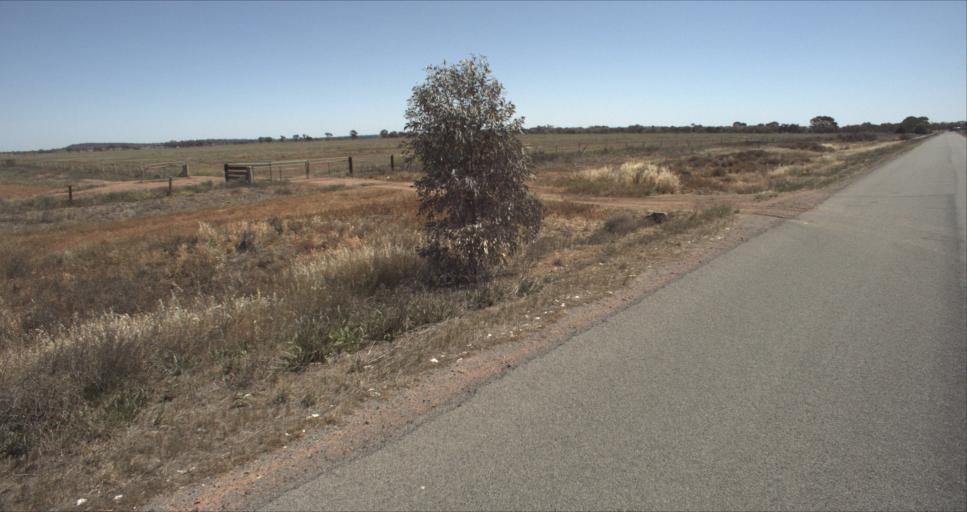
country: AU
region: New South Wales
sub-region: Leeton
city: Leeton
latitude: -34.4358
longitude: 146.2987
